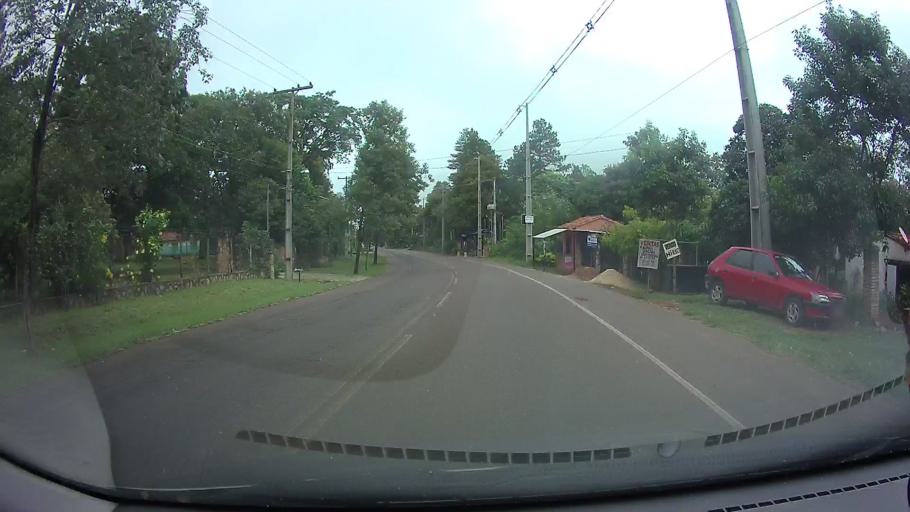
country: PY
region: Cordillera
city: Altos
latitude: -25.2906
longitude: -57.2685
